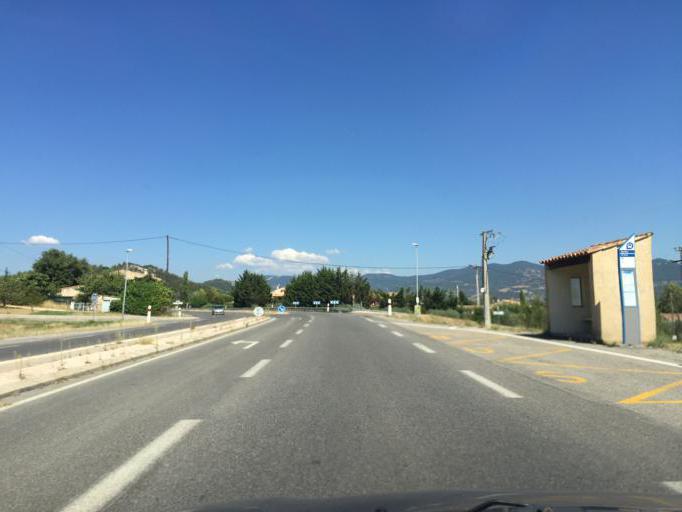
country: FR
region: Provence-Alpes-Cote d'Azur
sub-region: Departement des Alpes-de-Haute-Provence
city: Les Mees
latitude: 44.0624
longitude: 5.9770
